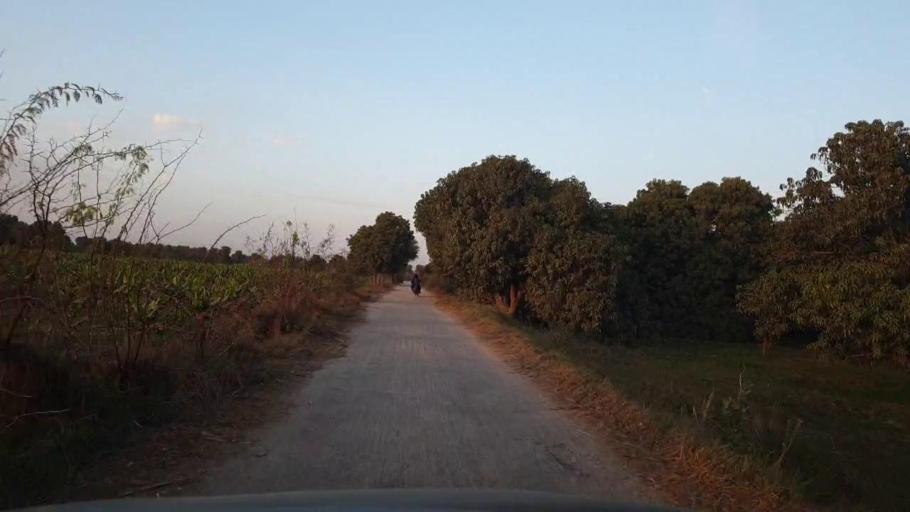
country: PK
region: Sindh
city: Matiari
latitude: 25.5907
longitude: 68.4768
